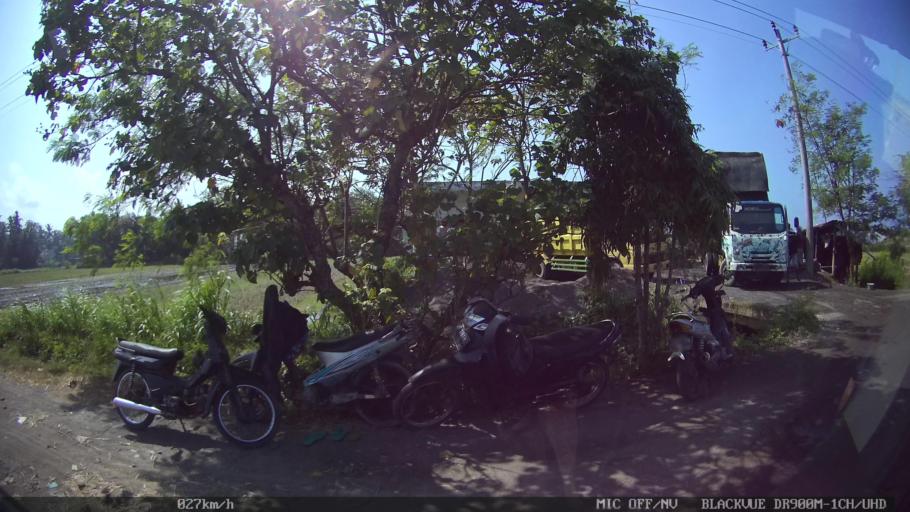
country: ID
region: Daerah Istimewa Yogyakarta
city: Srandakan
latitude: -7.9687
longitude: 110.2120
